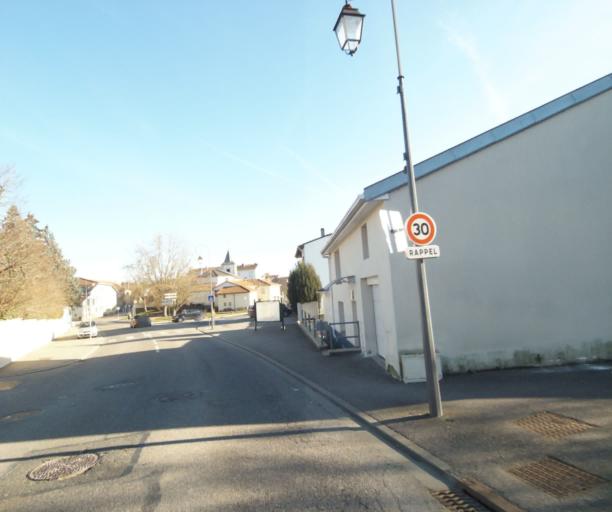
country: FR
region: Lorraine
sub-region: Departement de Meurthe-et-Moselle
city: Seichamps
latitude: 48.7173
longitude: 6.2647
